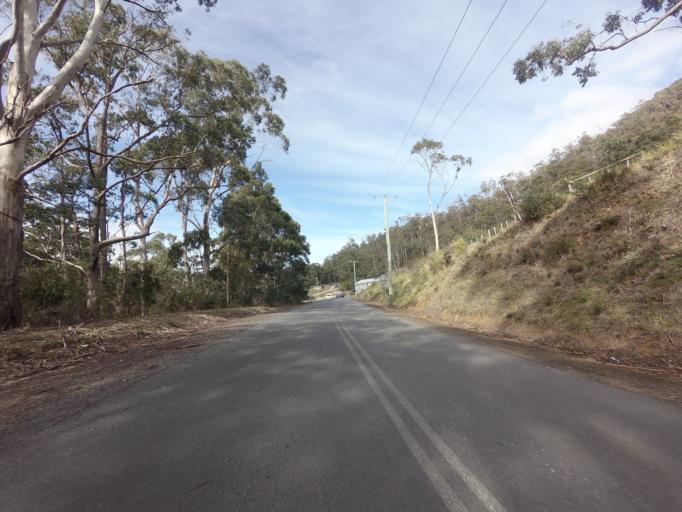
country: AU
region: Tasmania
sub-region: Clarence
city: Sandford
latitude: -43.1142
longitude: 147.7520
